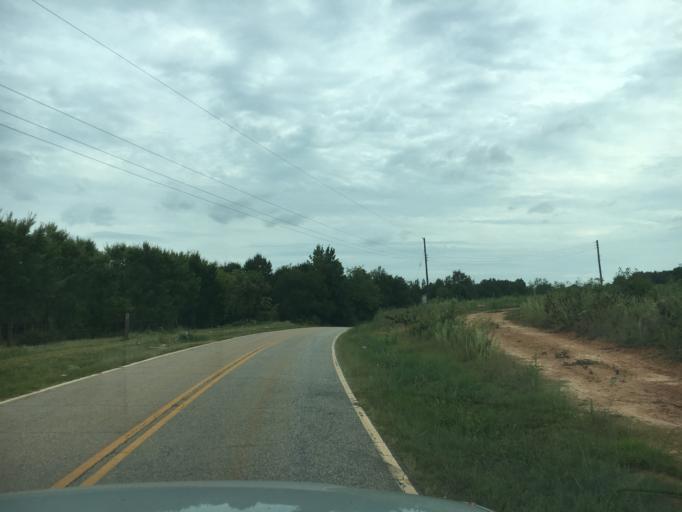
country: US
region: South Carolina
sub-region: Spartanburg County
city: Duncan
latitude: 34.9288
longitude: -82.1647
